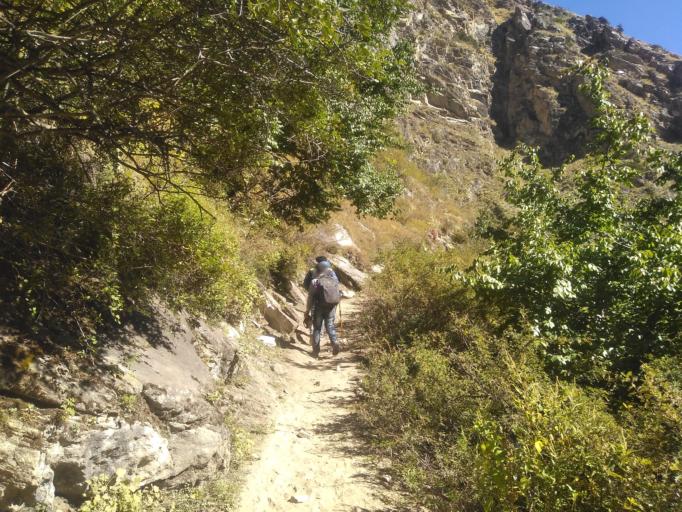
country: NP
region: Western Region
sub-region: Dhawalagiri Zone
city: Jomsom
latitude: 28.9409
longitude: 83.0574
